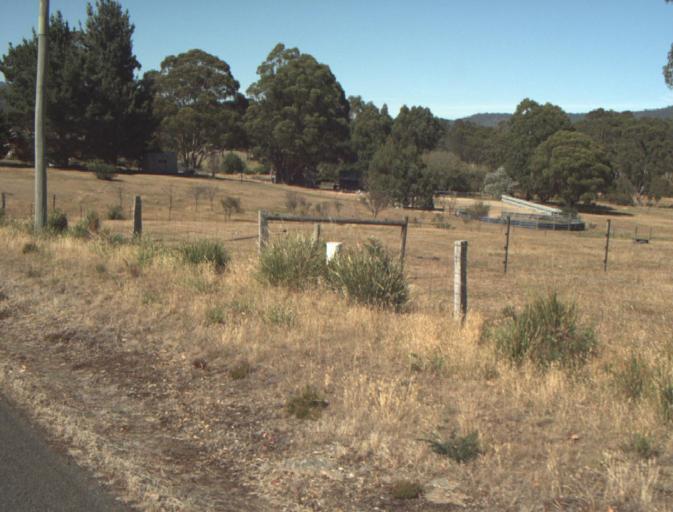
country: AU
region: Tasmania
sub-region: Launceston
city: Newstead
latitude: -41.3074
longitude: 147.3185
